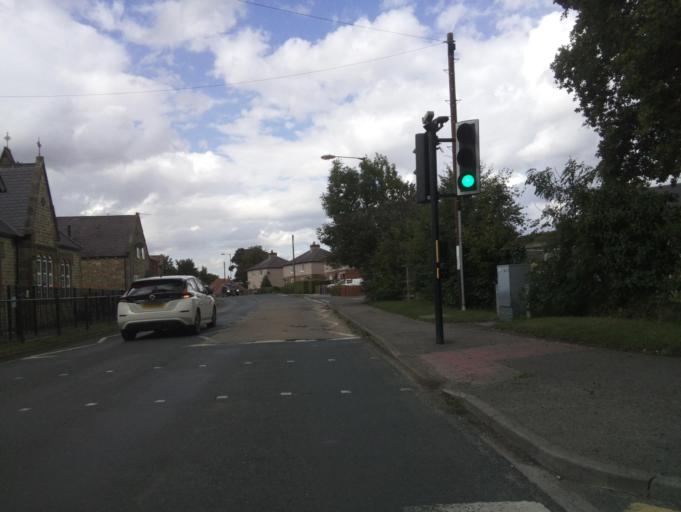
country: GB
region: England
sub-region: North Yorkshire
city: Ripon
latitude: 54.1886
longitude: -1.5627
